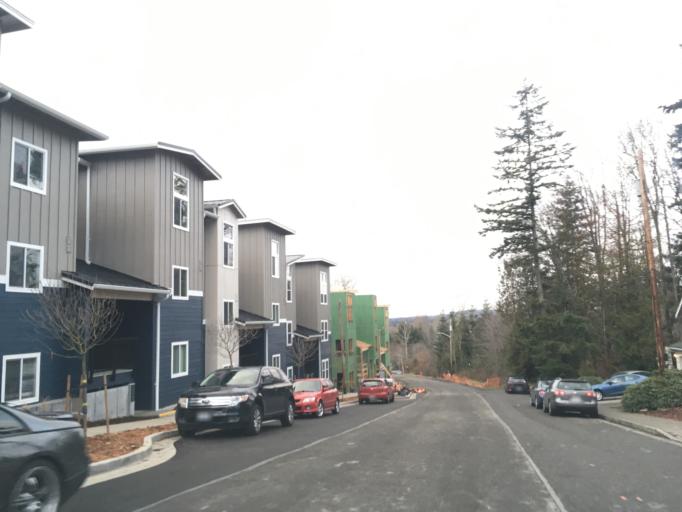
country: US
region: Washington
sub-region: Whatcom County
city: Bellingham
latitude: 48.7337
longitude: -122.4638
